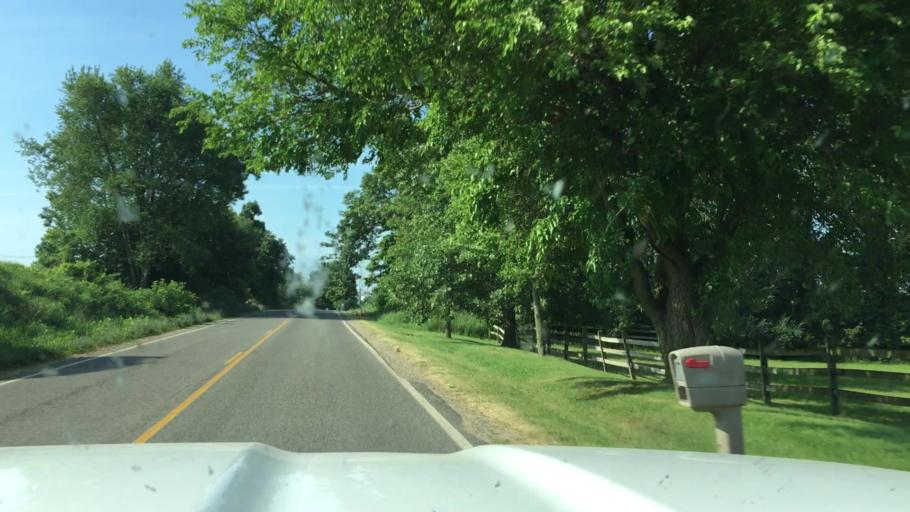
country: US
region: Michigan
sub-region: Barry County
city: Stony Point
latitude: 42.4431
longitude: -85.4545
